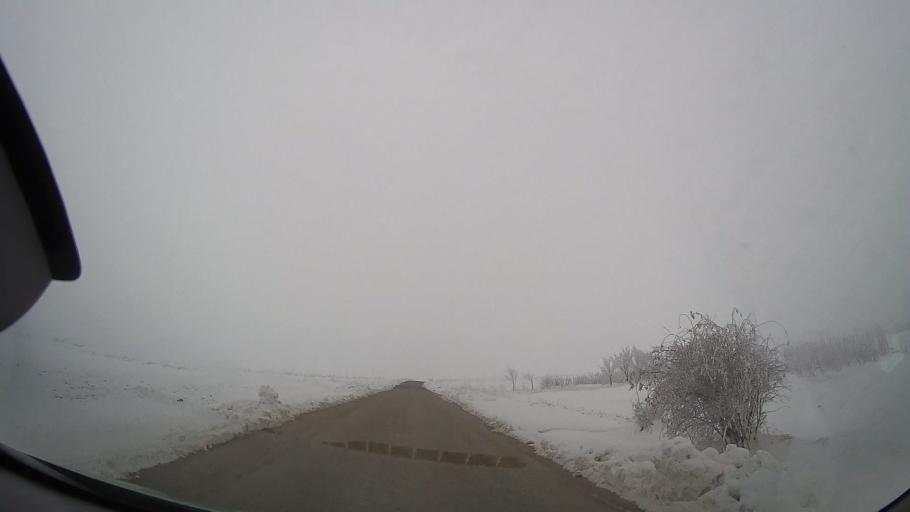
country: RO
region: Iasi
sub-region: Comuna Dagata
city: Dagata
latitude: 46.9079
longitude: 27.1971
